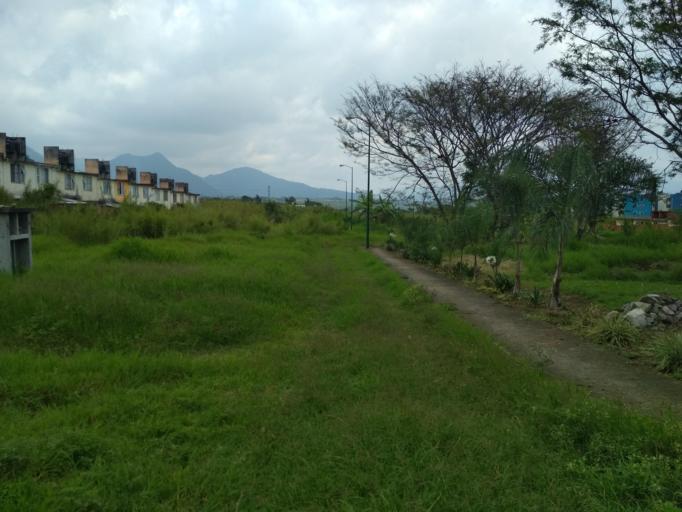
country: MX
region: Veracruz
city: Ixtac Zoquitlan
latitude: 18.8807
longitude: -97.0641
